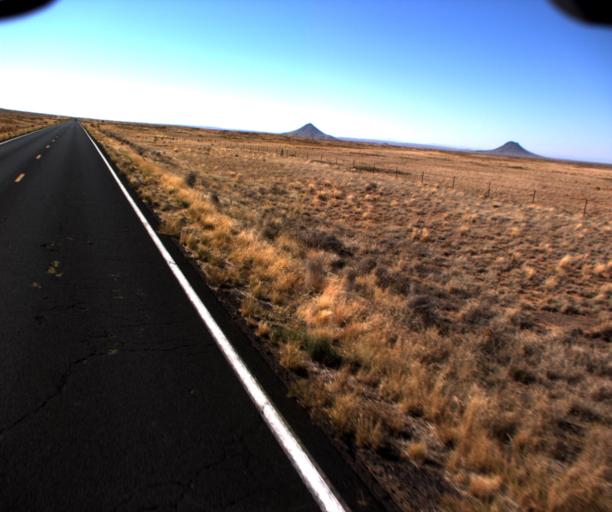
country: US
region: Arizona
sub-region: Navajo County
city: Dilkon
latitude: 35.4390
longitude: -110.4247
